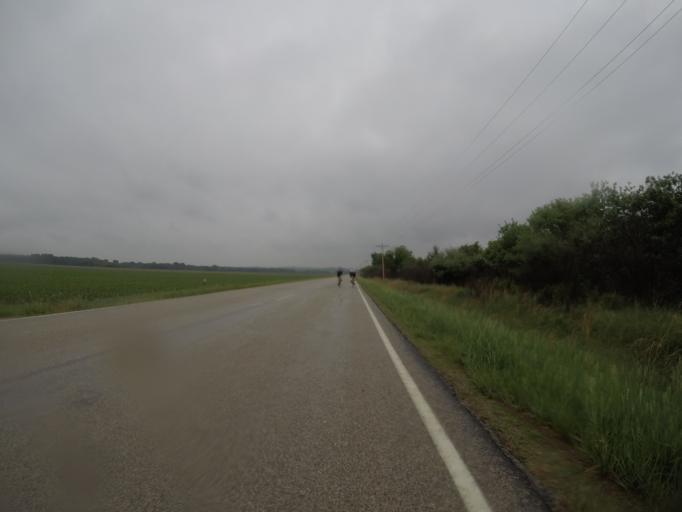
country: US
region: Kansas
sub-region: Pottawatomie County
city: Wamego
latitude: 39.3129
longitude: -96.2216
